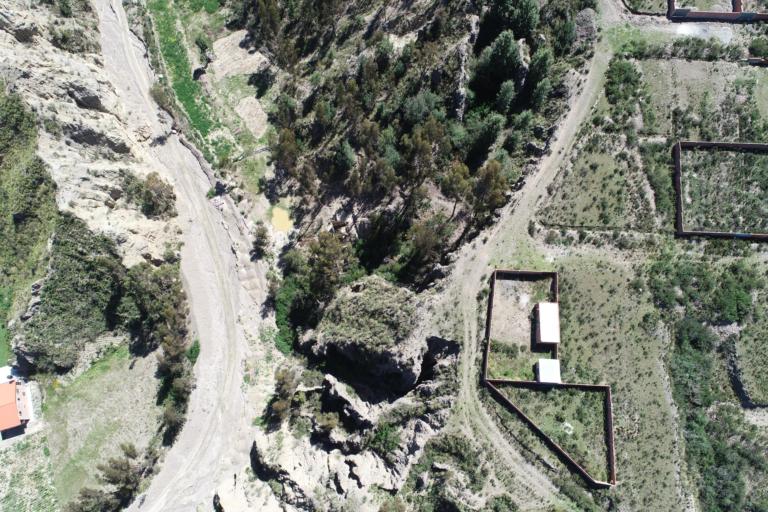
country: BO
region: La Paz
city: La Paz
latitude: -16.5061
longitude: -68.0591
